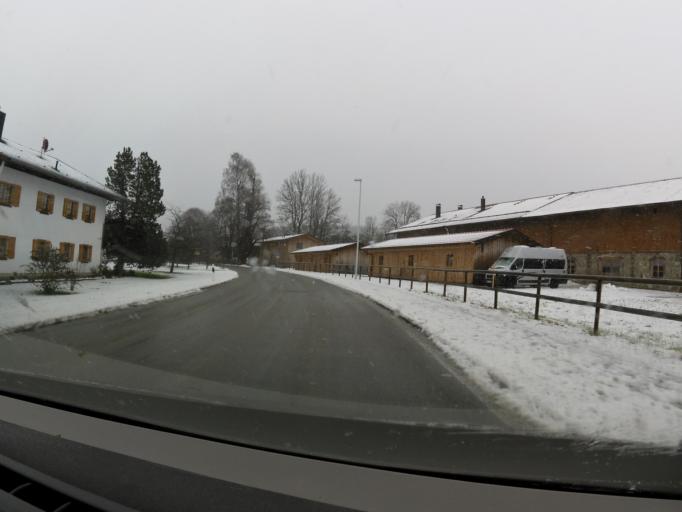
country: DE
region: Bavaria
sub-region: Upper Bavaria
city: Gmund am Tegernsee
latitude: 47.7557
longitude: 11.7119
